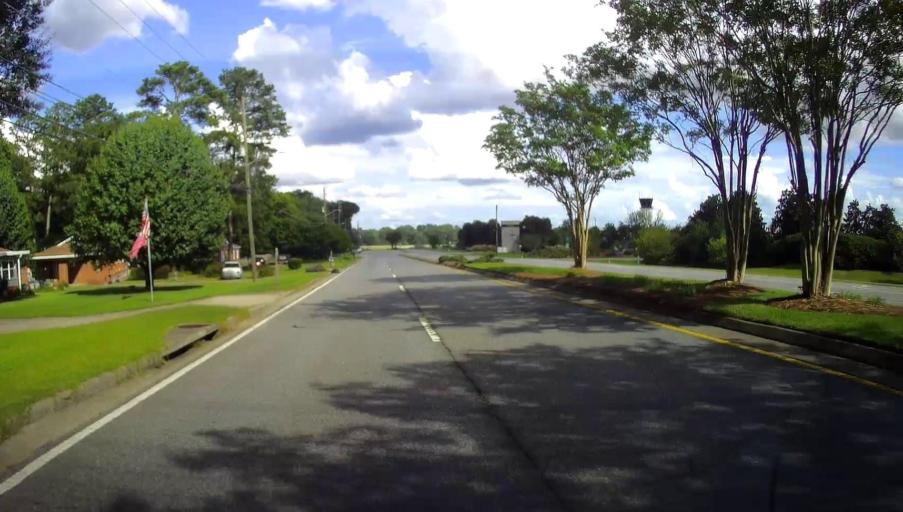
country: US
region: Georgia
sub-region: Muscogee County
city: Columbus
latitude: 32.5210
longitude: -84.9419
